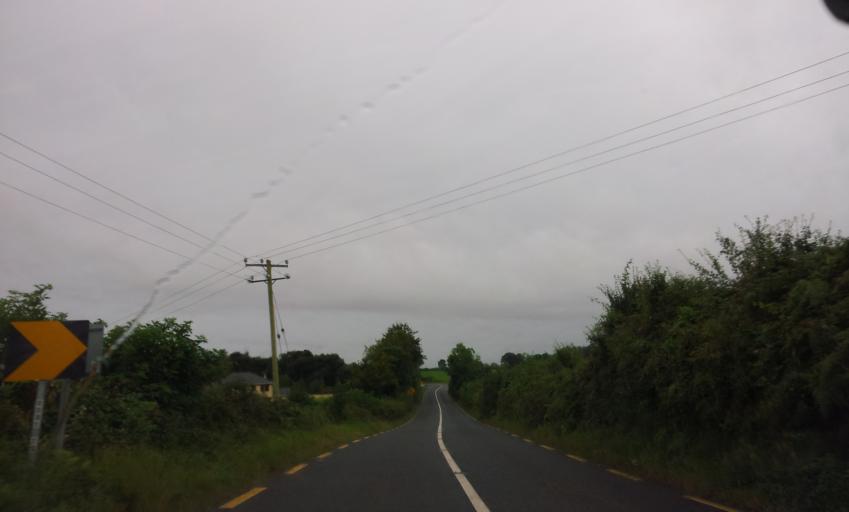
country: IE
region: Munster
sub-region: County Cork
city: Mallow
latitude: 52.2176
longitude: -8.5033
